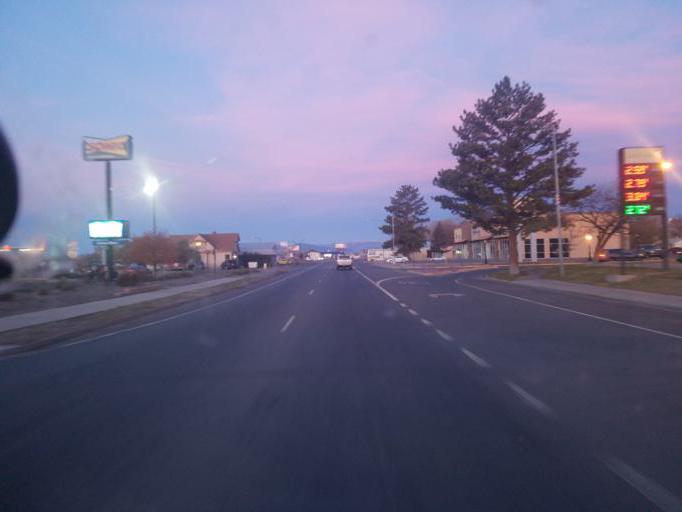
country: US
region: Colorado
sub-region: Alamosa County
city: Alamosa
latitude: 37.4682
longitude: -105.8755
